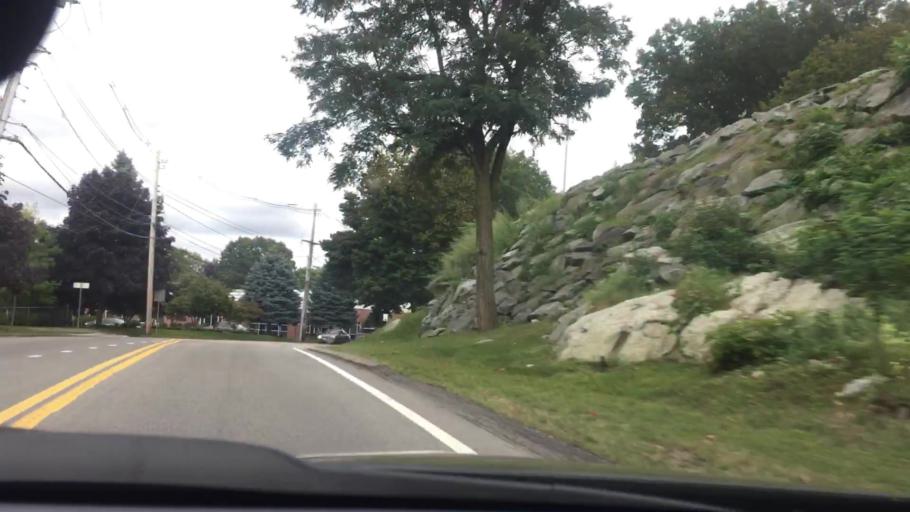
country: US
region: Massachusetts
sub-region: Norfolk County
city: Needham
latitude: 42.3045
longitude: -71.2185
